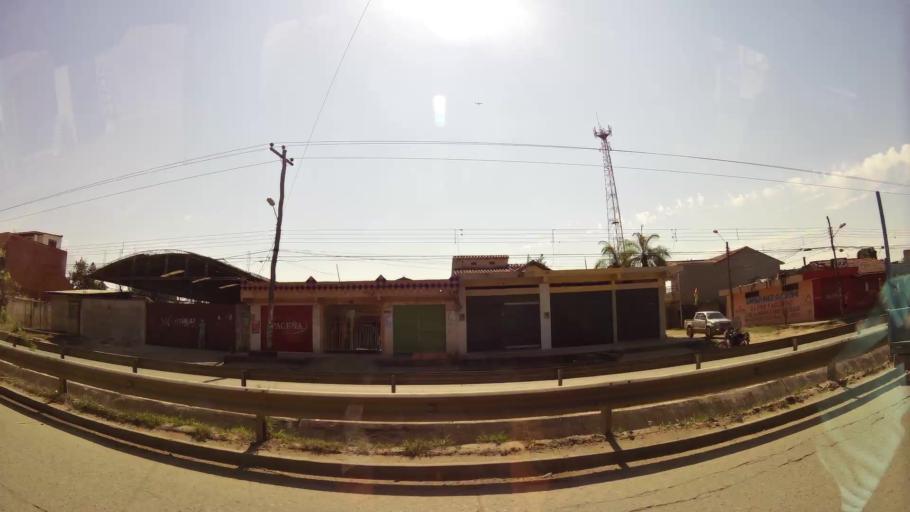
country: BO
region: Santa Cruz
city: Santa Cruz de la Sierra
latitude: -17.7509
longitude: -63.1280
